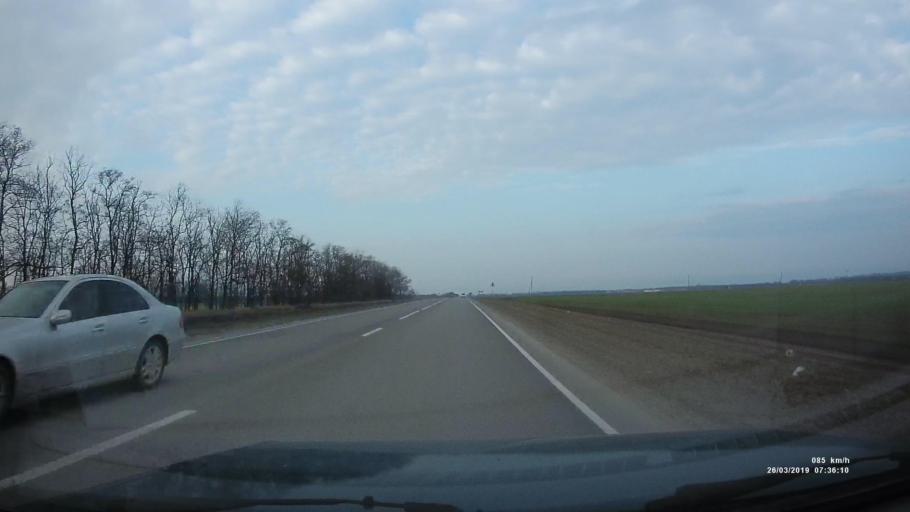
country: RU
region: Rostov
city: Novobessergenovka
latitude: 47.2059
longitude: 38.7253
